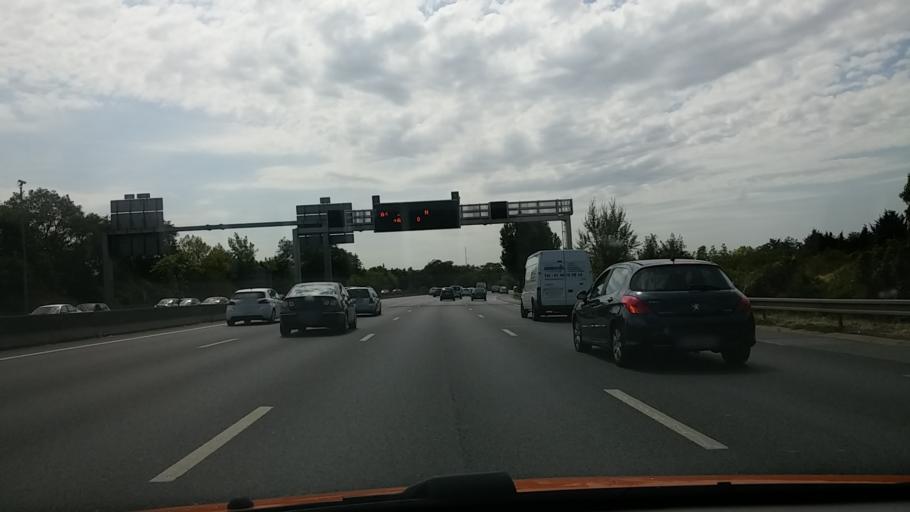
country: FR
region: Ile-de-France
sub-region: Departement du Val-de-Marne
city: Bry-sur-Marne
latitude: 48.8293
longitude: 2.5280
